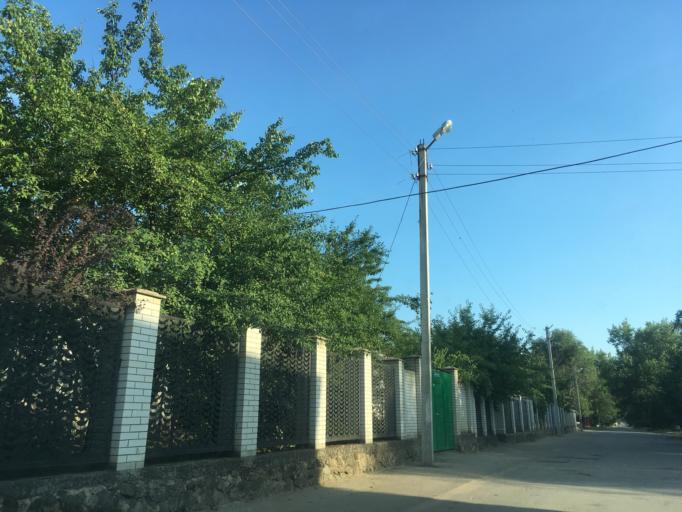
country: RU
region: Rostov
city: Masalovka
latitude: 48.4043
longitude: 40.2786
